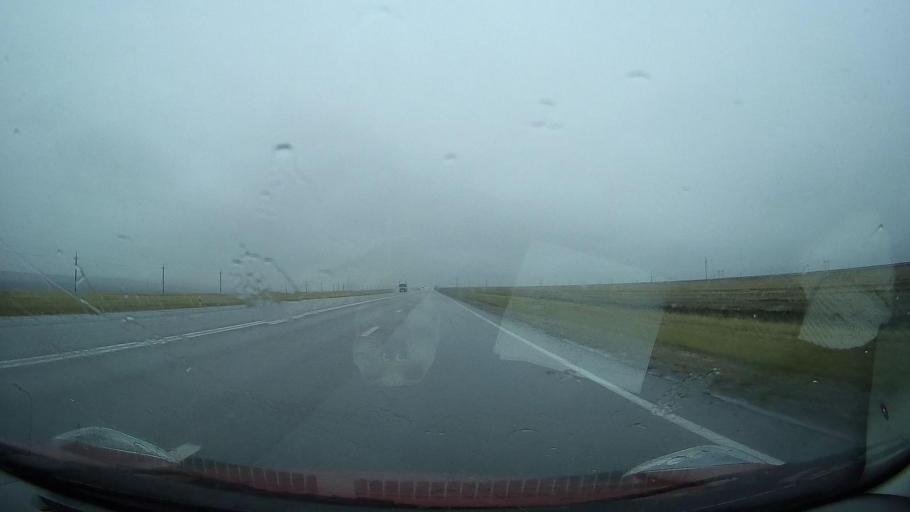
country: RU
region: Stavropol'skiy
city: Kursavka
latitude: 44.5808
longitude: 42.2440
